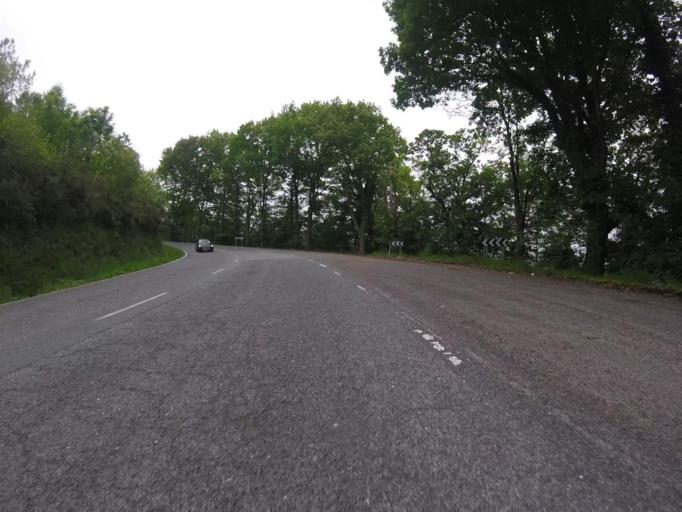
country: ES
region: Navarre
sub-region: Provincia de Navarra
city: Zugarramurdi
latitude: 43.2634
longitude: -1.4893
